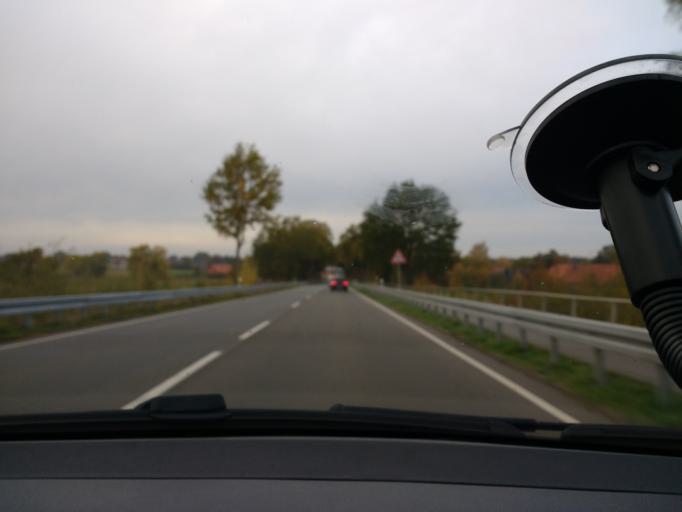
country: DE
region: Lower Saxony
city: Calberlah
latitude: 52.4168
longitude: 10.6383
